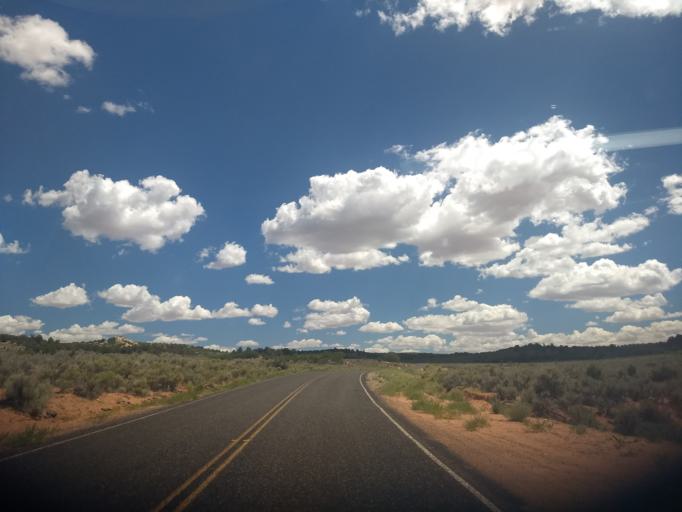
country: US
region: Utah
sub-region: Kane County
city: Kanab
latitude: 37.1374
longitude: -112.6760
